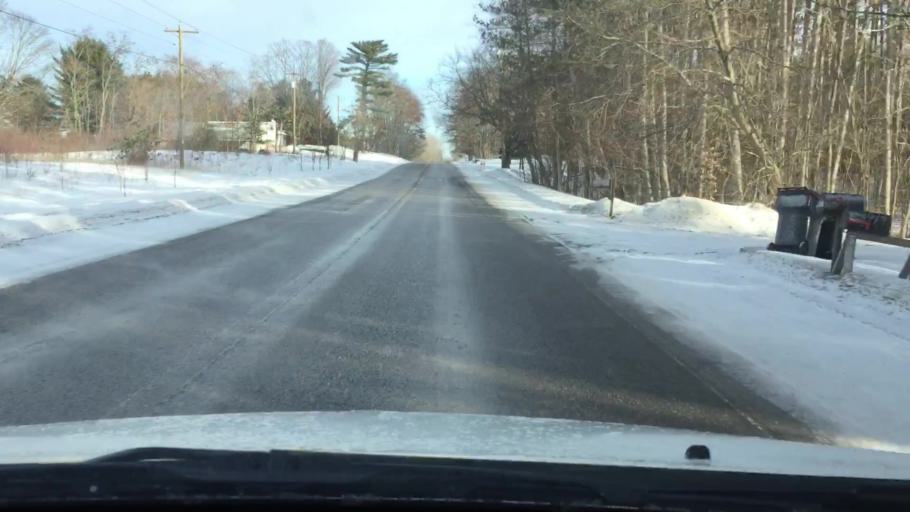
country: US
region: Michigan
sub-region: Kalkaska County
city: Kalkaska
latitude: 44.6412
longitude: -85.2738
